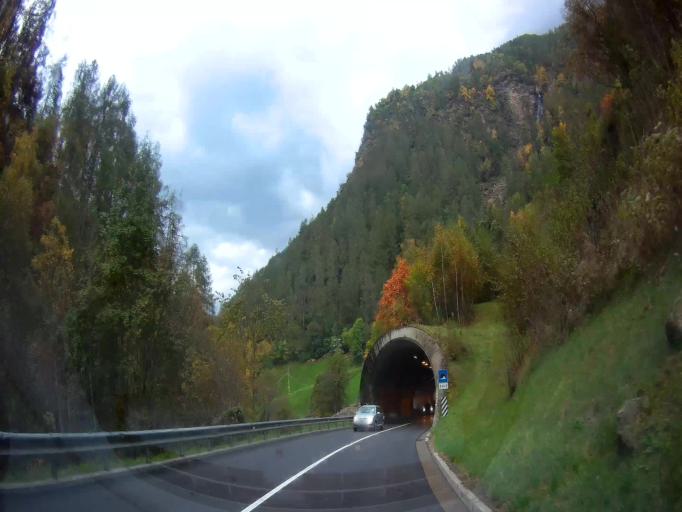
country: IT
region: Trentino-Alto Adige
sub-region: Bolzano
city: Certosa
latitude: 46.6870
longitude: 10.9309
